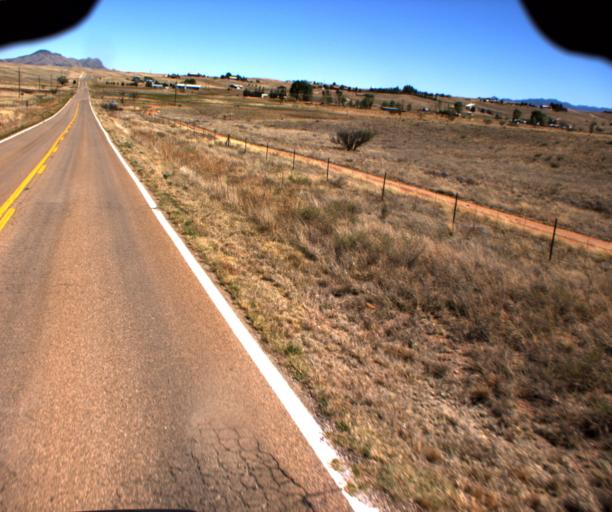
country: US
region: Arizona
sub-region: Cochise County
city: Huachuca City
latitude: 31.6735
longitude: -110.6203
